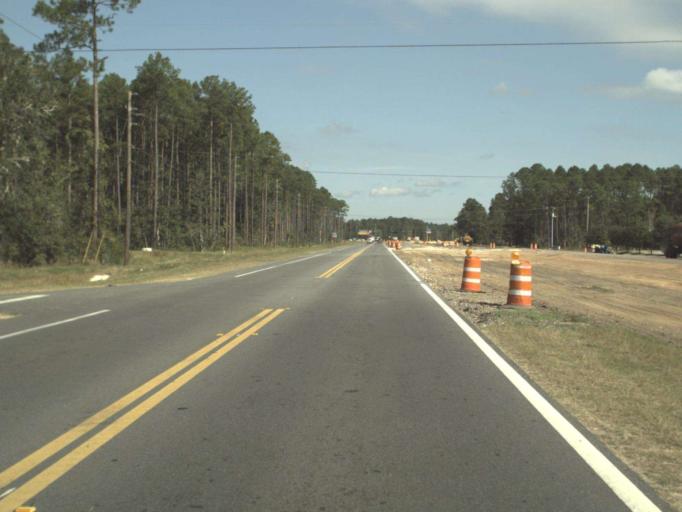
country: US
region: Florida
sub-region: Walton County
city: Freeport
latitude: 30.4594
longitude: -86.1313
